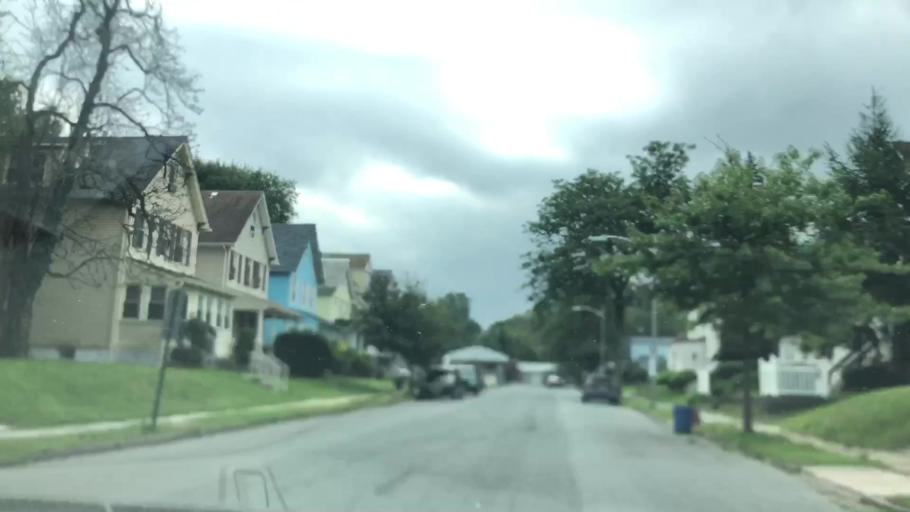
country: US
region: New Jersey
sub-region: Essex County
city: East Orange
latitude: 40.7824
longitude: -74.2061
